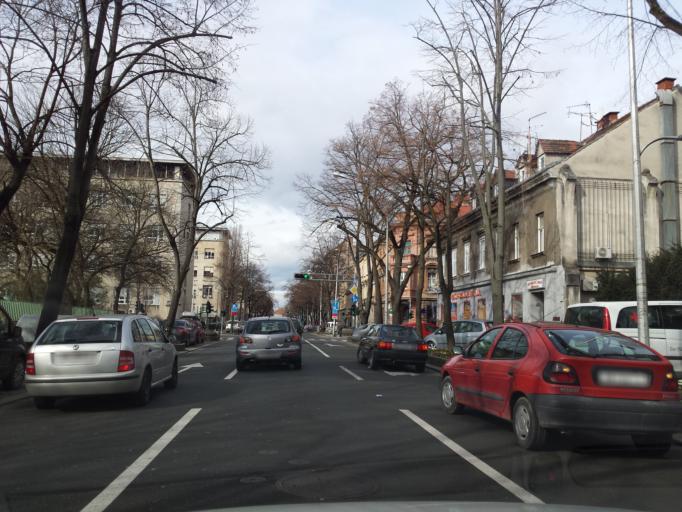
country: HR
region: Grad Zagreb
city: Zagreb - Centar
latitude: 45.8092
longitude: 15.9647
